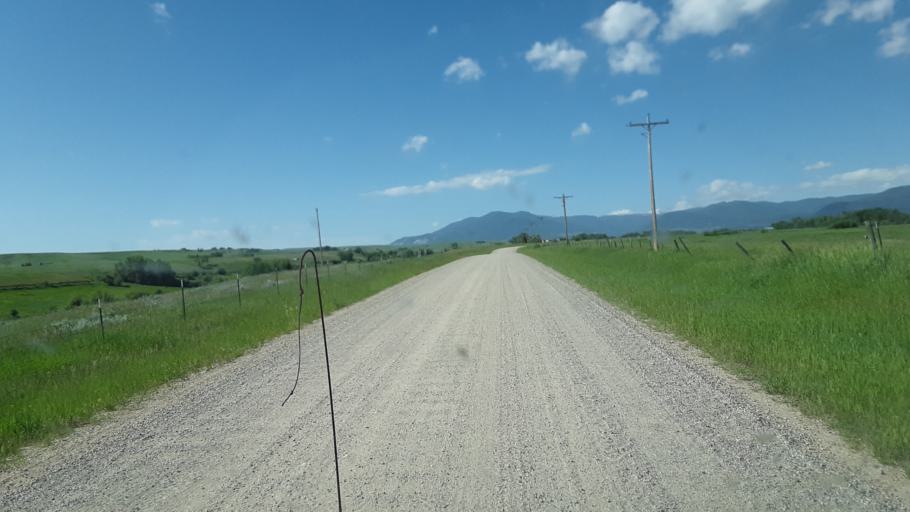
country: US
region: Montana
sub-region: Carbon County
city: Red Lodge
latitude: 45.2842
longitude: -109.1897
